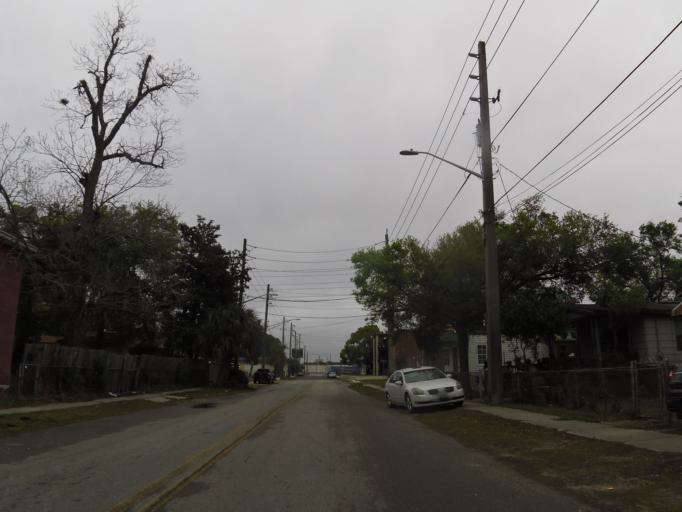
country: US
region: Florida
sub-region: Duval County
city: Jacksonville
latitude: 30.3365
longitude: -81.6402
